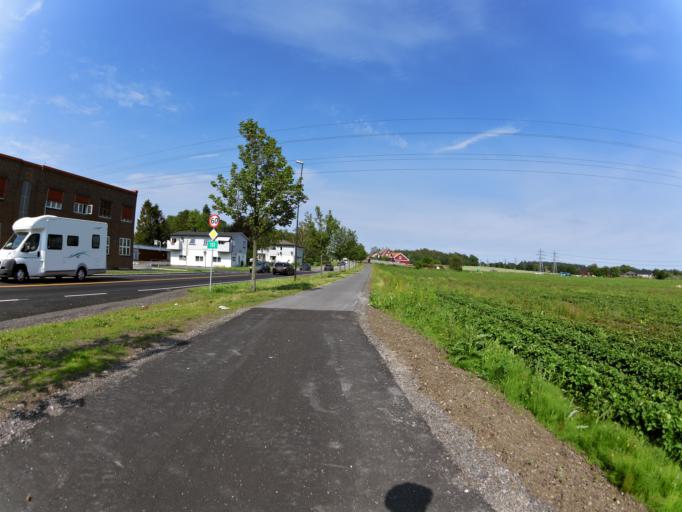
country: NO
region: Ostfold
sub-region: Sarpsborg
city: Sarpsborg
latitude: 59.2660
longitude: 11.1221
